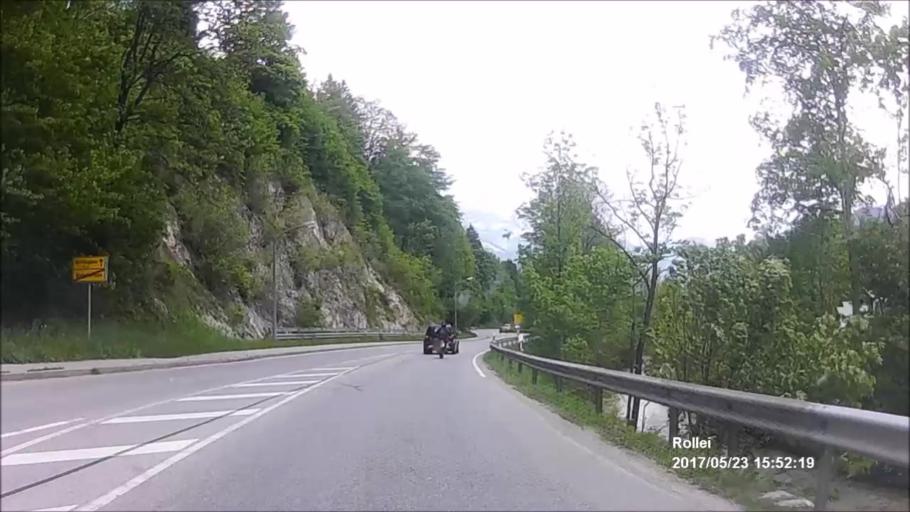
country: DE
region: Bavaria
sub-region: Upper Bavaria
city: Bischofswiesen
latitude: 47.6467
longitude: 12.9696
